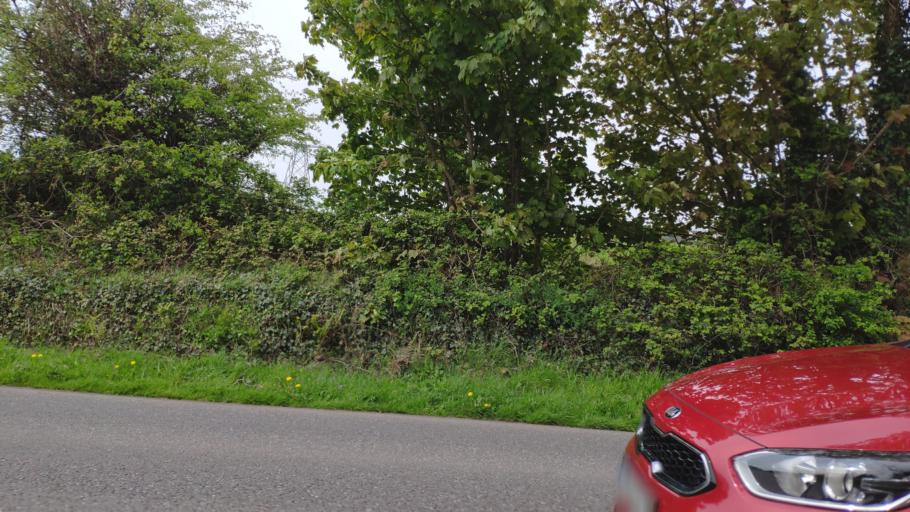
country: IE
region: Munster
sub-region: County Cork
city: Cork
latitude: 51.9230
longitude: -8.4560
